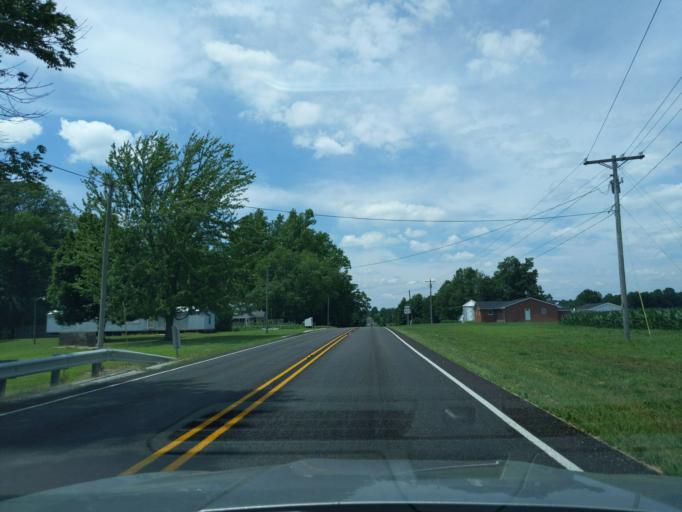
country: US
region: Indiana
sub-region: Decatur County
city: Greensburg
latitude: 39.2791
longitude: -85.4022
